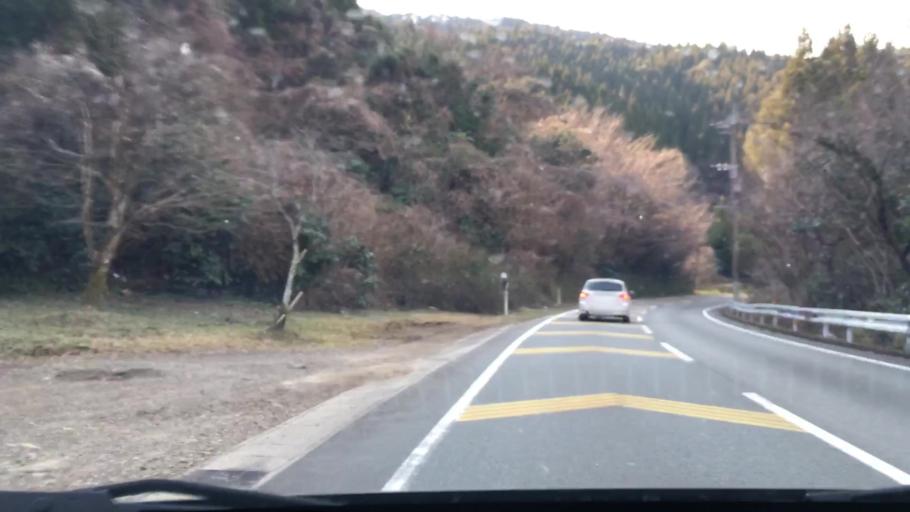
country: JP
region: Miyazaki
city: Miyazaki-shi
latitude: 31.7902
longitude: 131.3173
